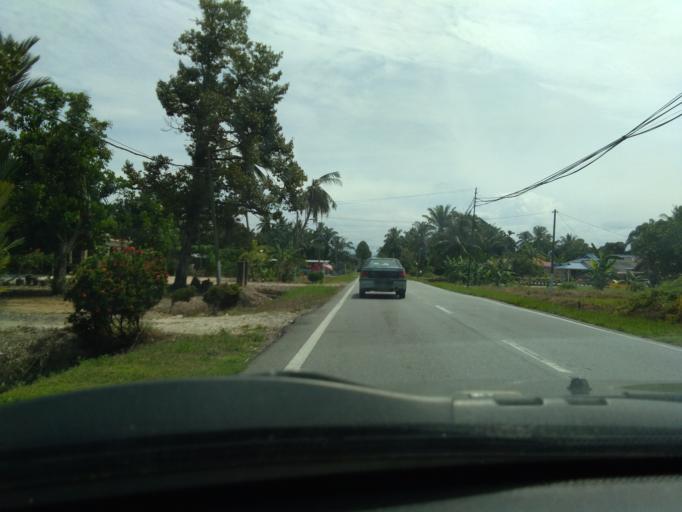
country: MY
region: Perak
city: Bagan Serai
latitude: 5.0472
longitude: 100.5822
